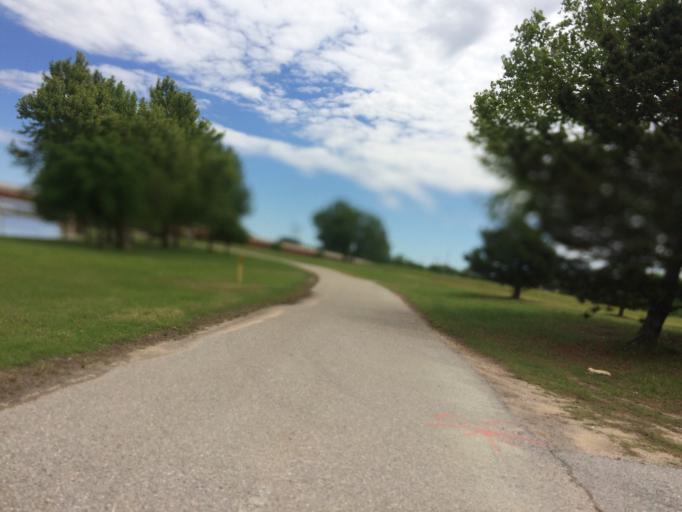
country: US
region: Oklahoma
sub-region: Oklahoma County
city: Oklahoma City
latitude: 35.4485
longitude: -97.5111
